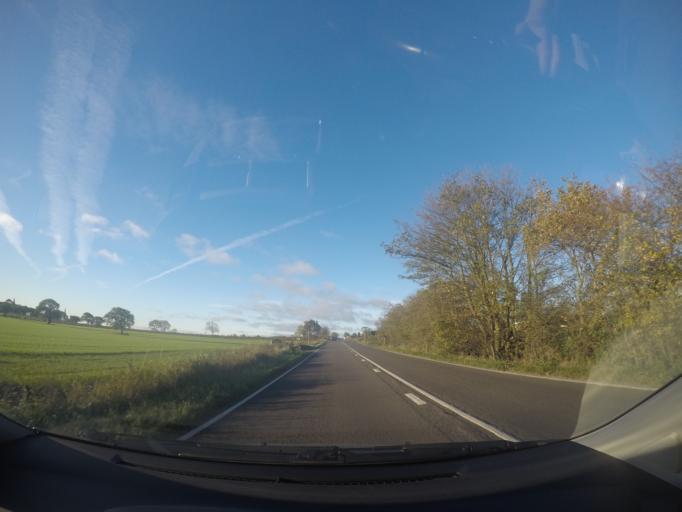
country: GB
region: England
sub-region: City and Borough of Leeds
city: Thorner
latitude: 53.8429
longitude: -1.4190
